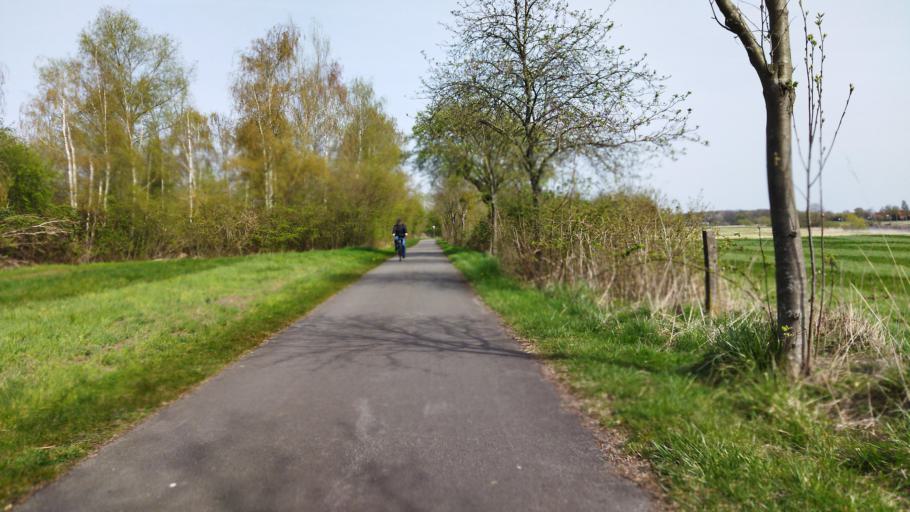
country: DE
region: North Rhine-Westphalia
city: Porta Westfalica
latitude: 52.2621
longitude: 8.9193
